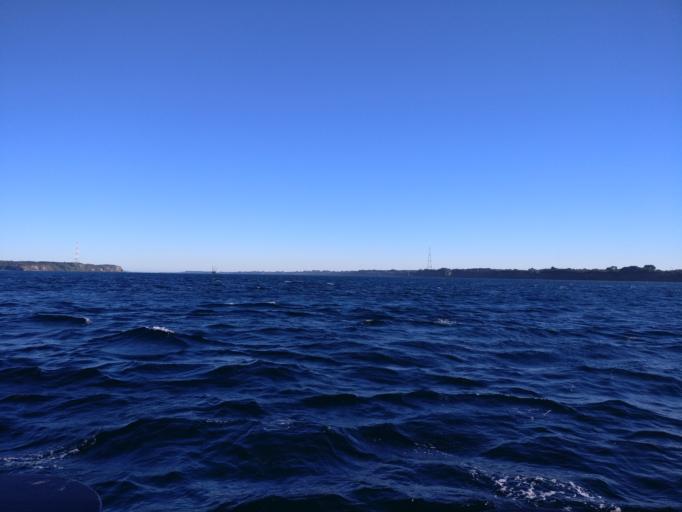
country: CL
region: Los Lagos
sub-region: Provincia de Chiloe
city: Ancud
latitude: -41.8114
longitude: -73.4828
